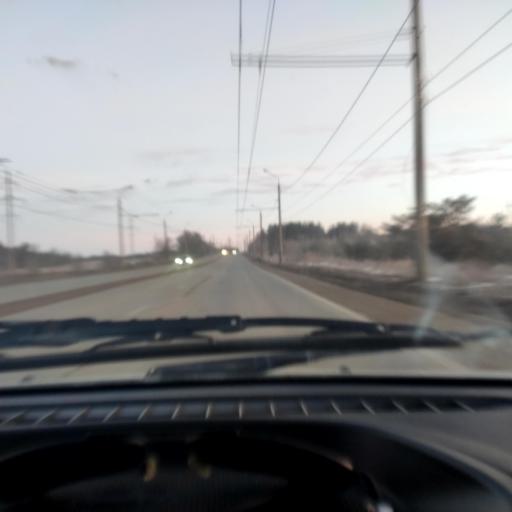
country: RU
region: Samara
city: Zhigulevsk
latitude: 53.5034
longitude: 49.5154
